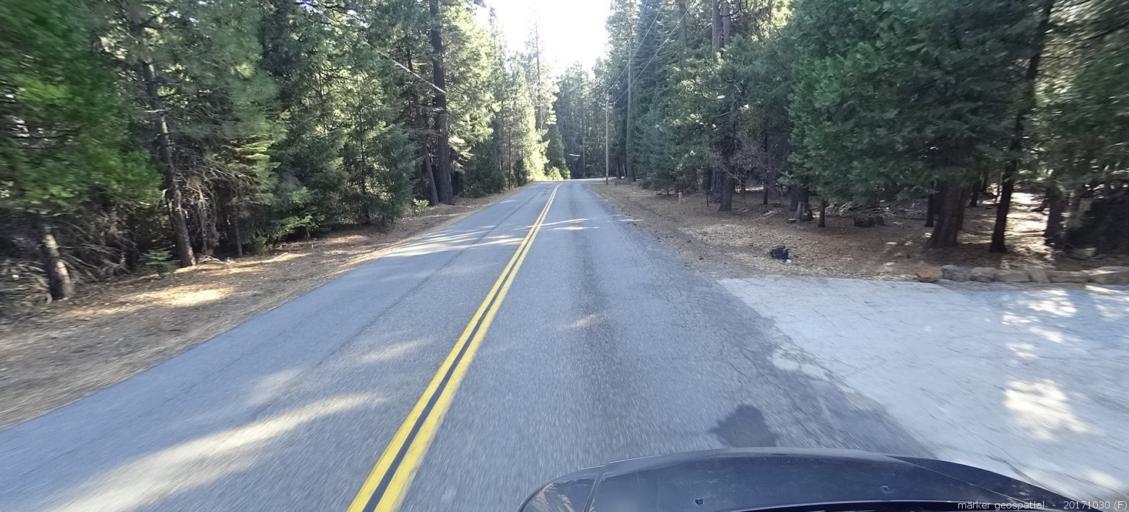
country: US
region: California
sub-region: Shasta County
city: Shingletown
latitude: 40.5264
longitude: -121.7470
